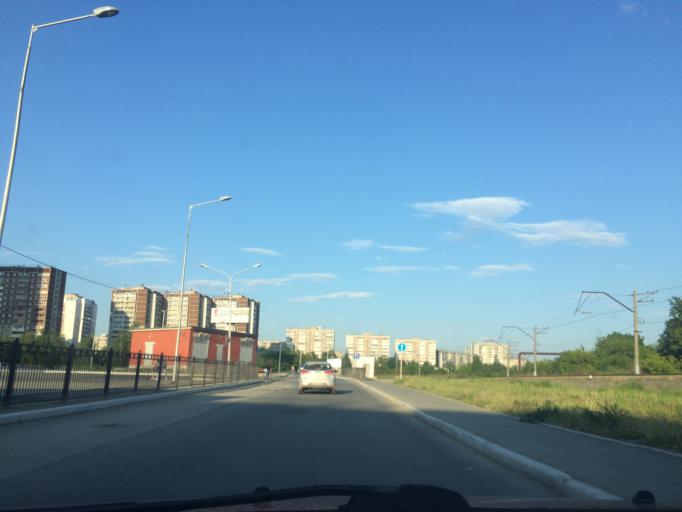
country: RU
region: Sverdlovsk
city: Yekaterinburg
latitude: 56.8288
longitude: 60.6752
